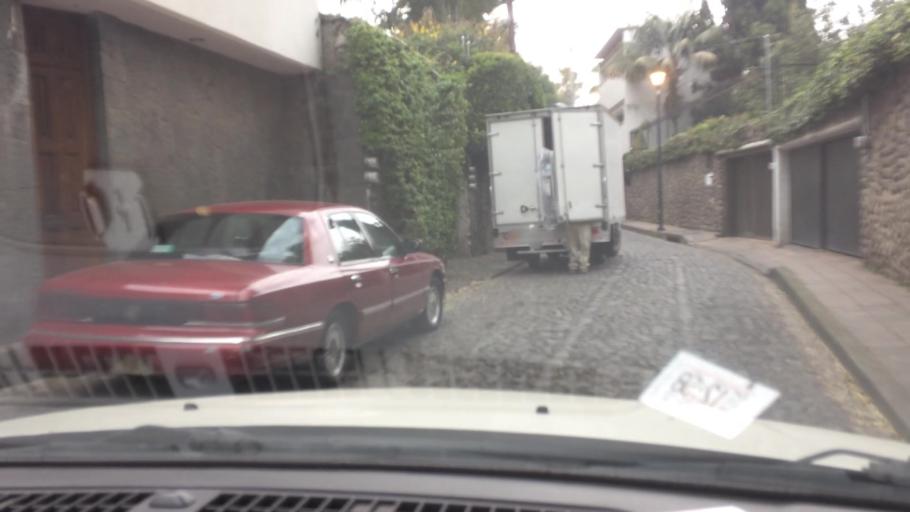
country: MX
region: Mexico City
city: Alvaro Obregon
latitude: 19.3529
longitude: -99.1946
